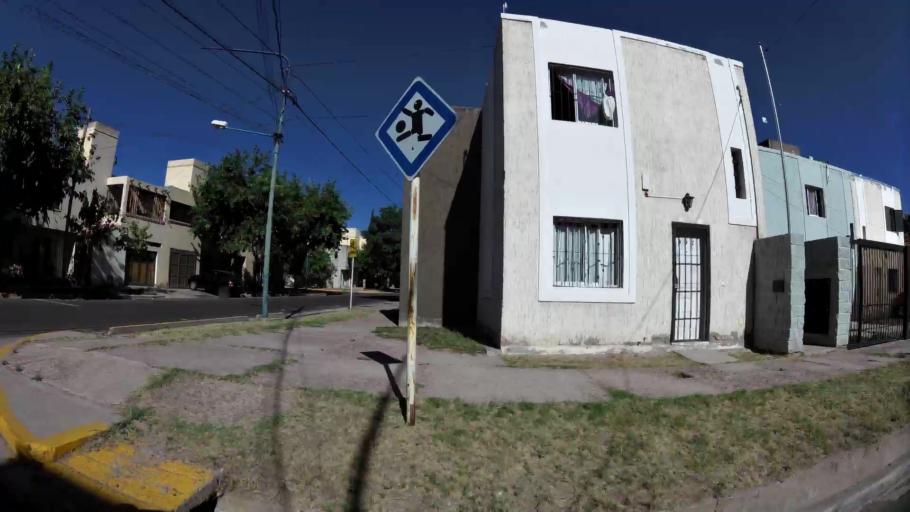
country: AR
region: Mendoza
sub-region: Departamento de Godoy Cruz
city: Godoy Cruz
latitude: -32.9358
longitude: -68.8594
